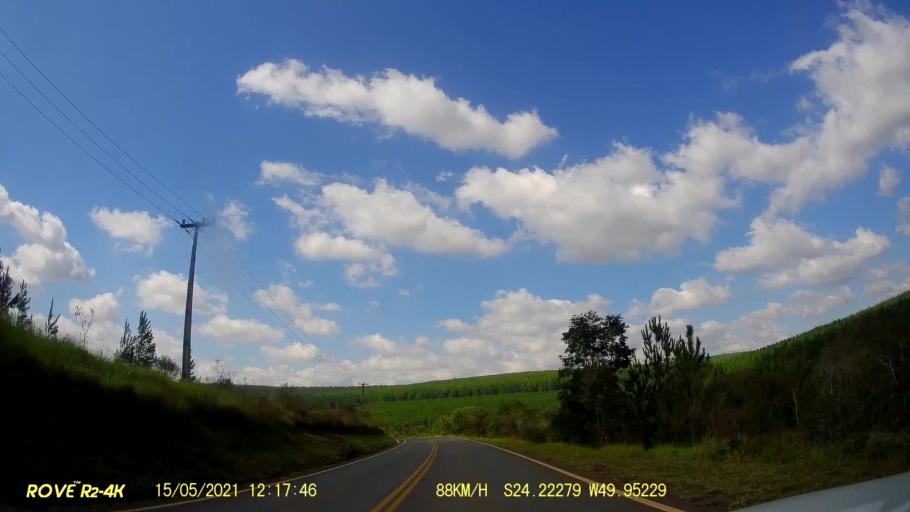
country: BR
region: Parana
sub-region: Jaguariaiva
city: Jaguariaiva
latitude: -24.2227
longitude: -49.9528
